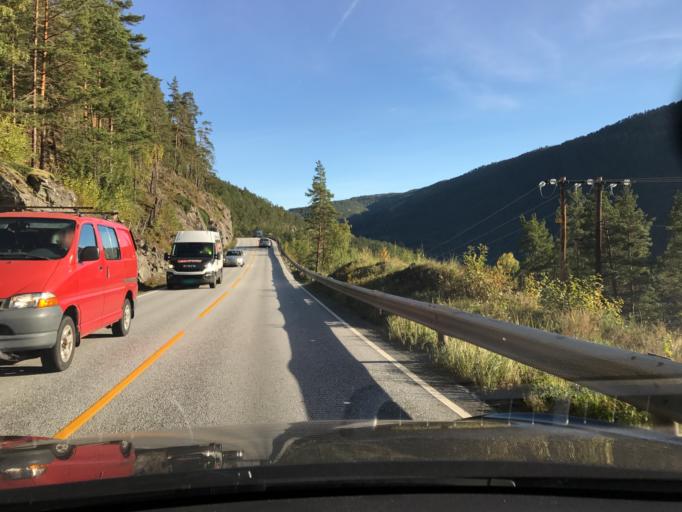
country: NO
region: Sogn og Fjordane
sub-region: Sogndal
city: Sogndalsfjora
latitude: 61.2106
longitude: 7.1507
